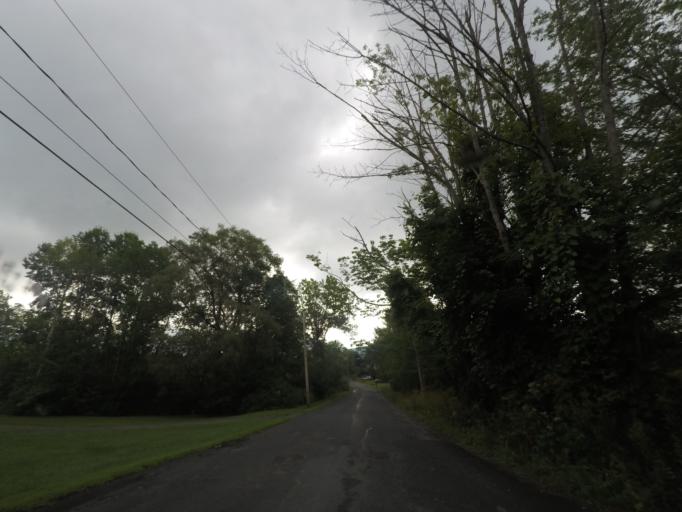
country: US
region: Massachusetts
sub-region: Berkshire County
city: Pittsfield
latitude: 42.4247
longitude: -73.3140
